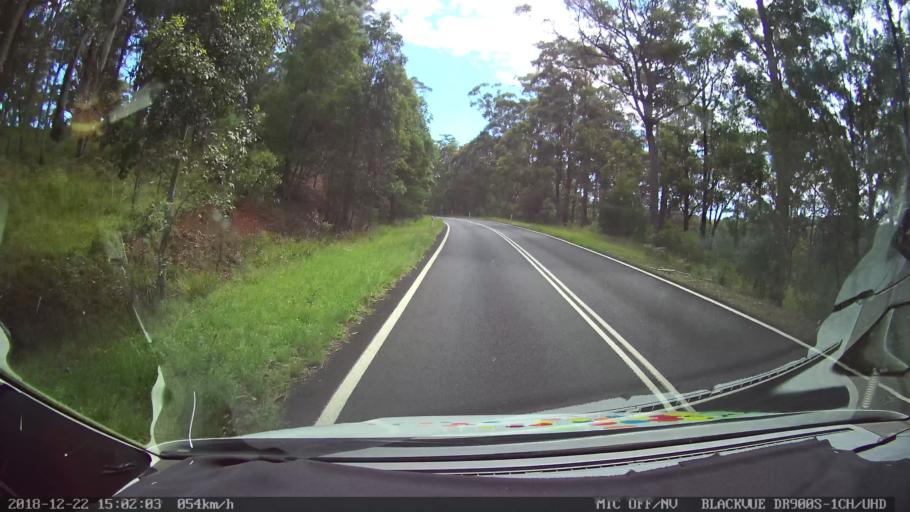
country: AU
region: New South Wales
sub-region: Bellingen
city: Dorrigo
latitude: -30.2592
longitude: 152.4544
